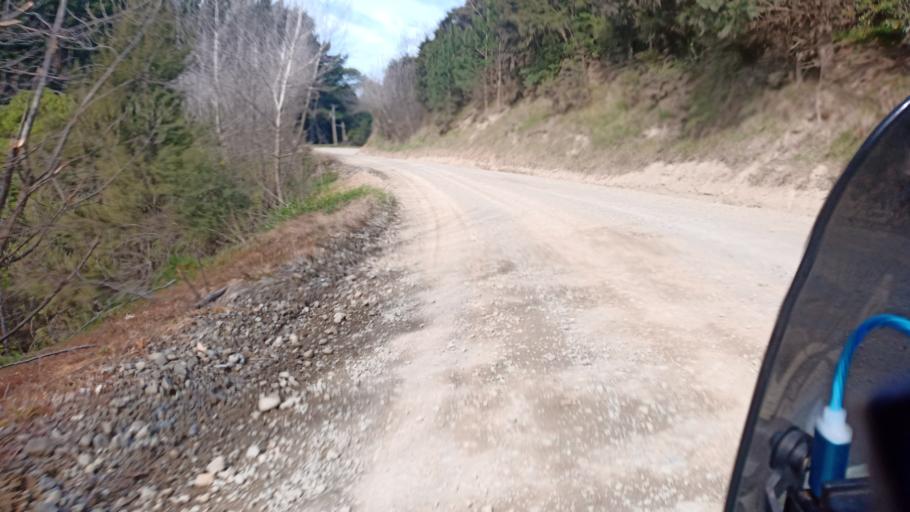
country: NZ
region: Gisborne
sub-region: Gisborne District
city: Gisborne
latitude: -38.1310
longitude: 178.1868
